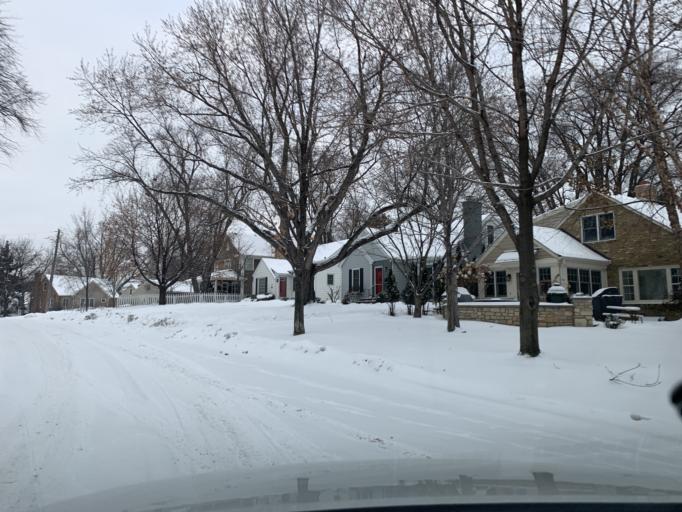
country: US
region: Minnesota
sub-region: Hennepin County
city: Saint Louis Park
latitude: 44.9307
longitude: -93.3419
